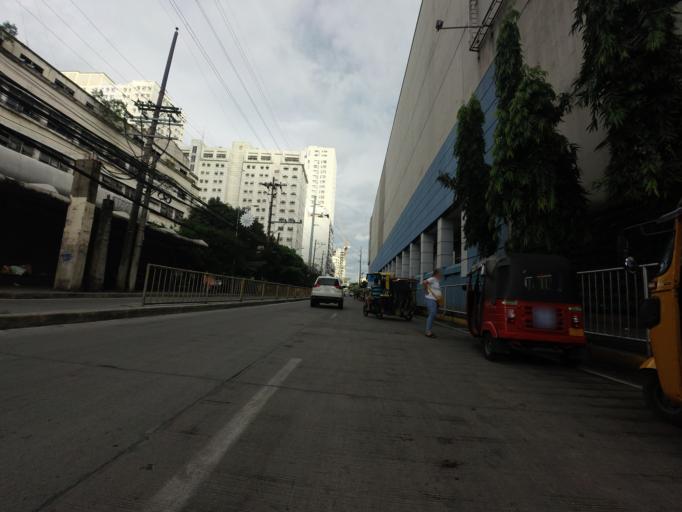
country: PH
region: Metro Manila
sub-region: City of Manila
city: Quiapo
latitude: 14.5904
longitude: 120.9825
